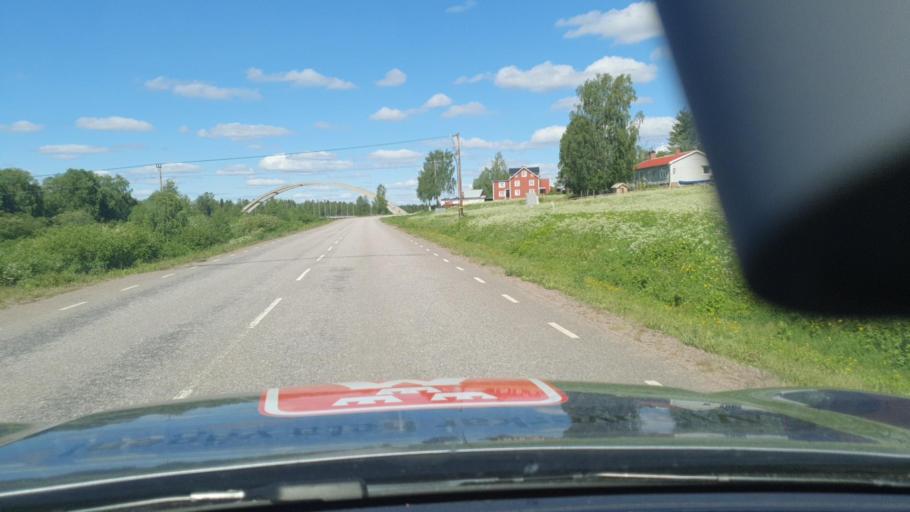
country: SE
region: Norrbotten
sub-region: Pajala Kommun
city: Pajala
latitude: 67.1651
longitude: 22.6189
